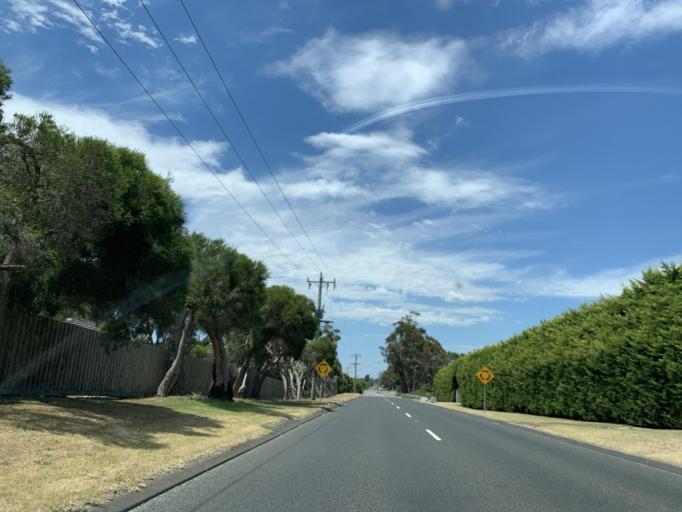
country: AU
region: Victoria
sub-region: Mornington Peninsula
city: Tyabb
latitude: -38.2386
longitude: 145.2111
